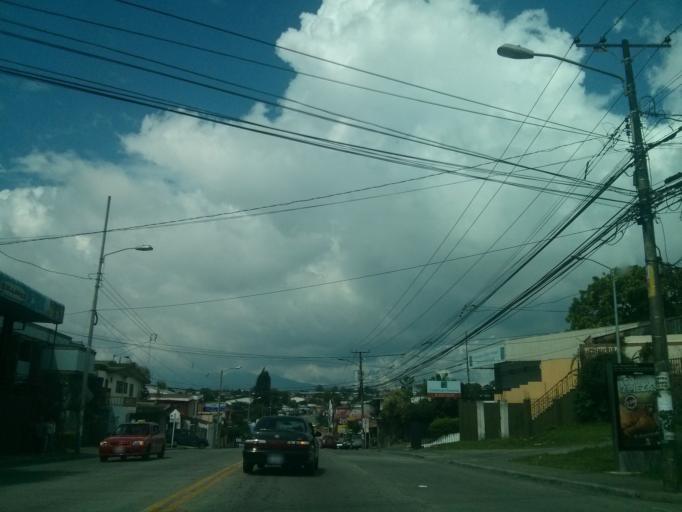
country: CR
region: San Jose
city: San Pedro
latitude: 9.9117
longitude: -84.0572
